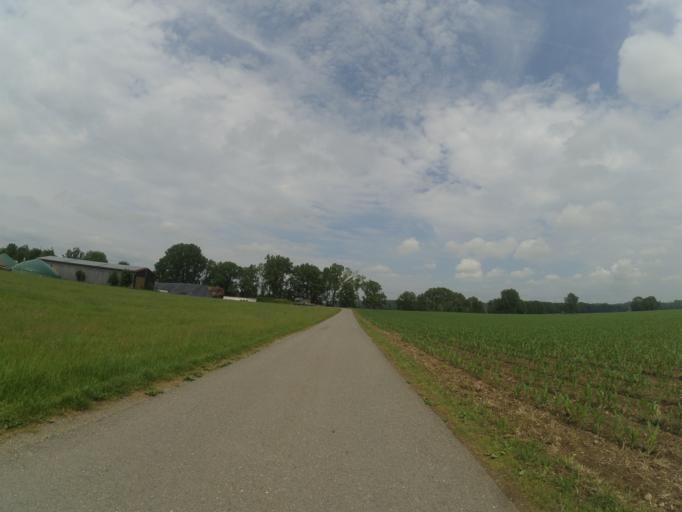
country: DE
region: Baden-Wuerttemberg
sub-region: Tuebingen Region
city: Leutkirch im Allgau
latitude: 47.7982
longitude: 10.0186
